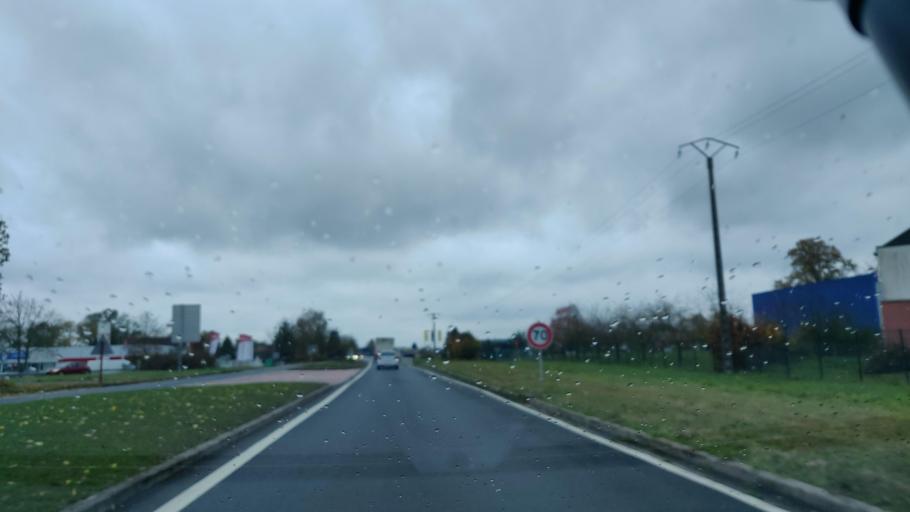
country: FR
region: Lorraine
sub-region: Departement de Meurthe-et-Moselle
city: Chanteheux
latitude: 48.5695
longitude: 6.5346
